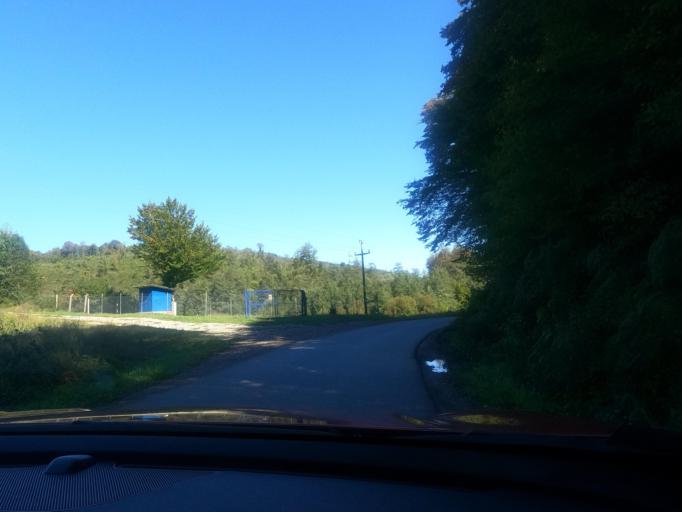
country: HR
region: Sisacko-Moslavacka
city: Petrinja
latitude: 45.3934
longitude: 16.2422
